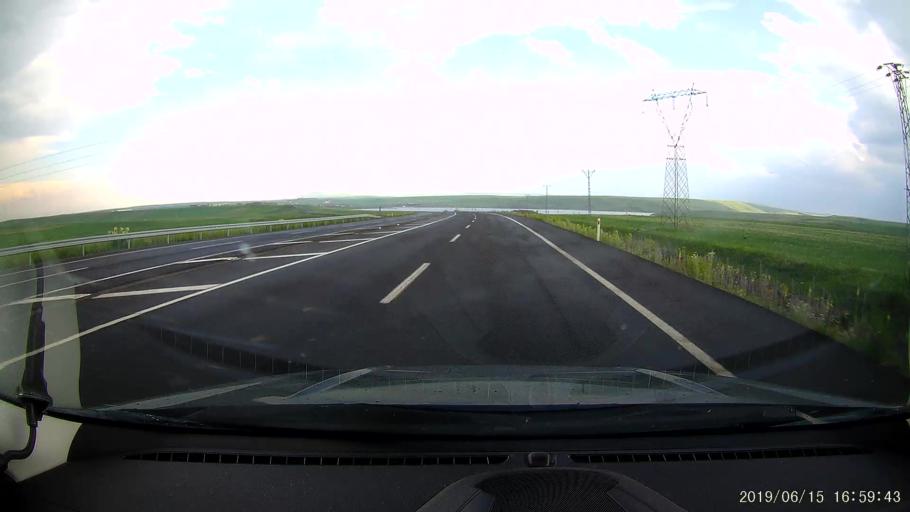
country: TR
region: Kars
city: Susuz
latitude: 40.7481
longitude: 43.1527
